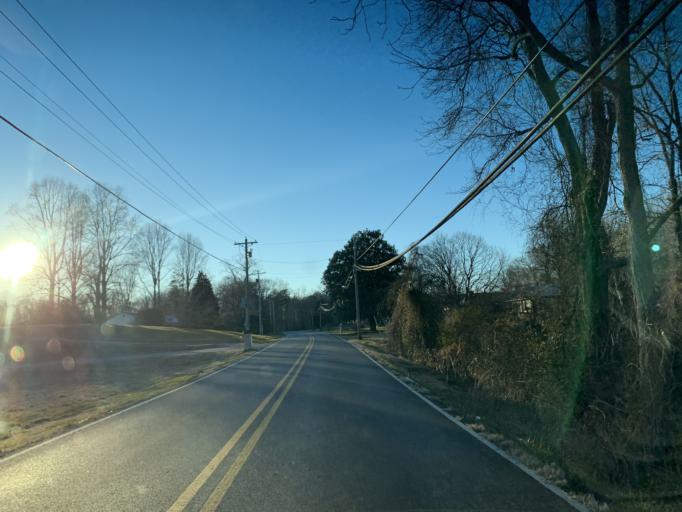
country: US
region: Maryland
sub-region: Saint Mary's County
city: Mechanicsville
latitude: 38.4674
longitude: -76.7352
